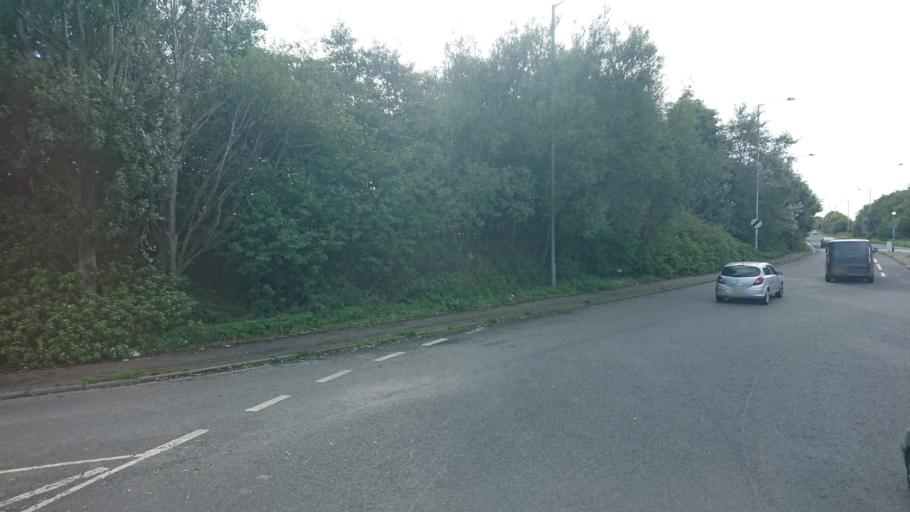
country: GB
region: England
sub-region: Lancashire
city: Morecambe
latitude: 54.0543
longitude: -2.8395
